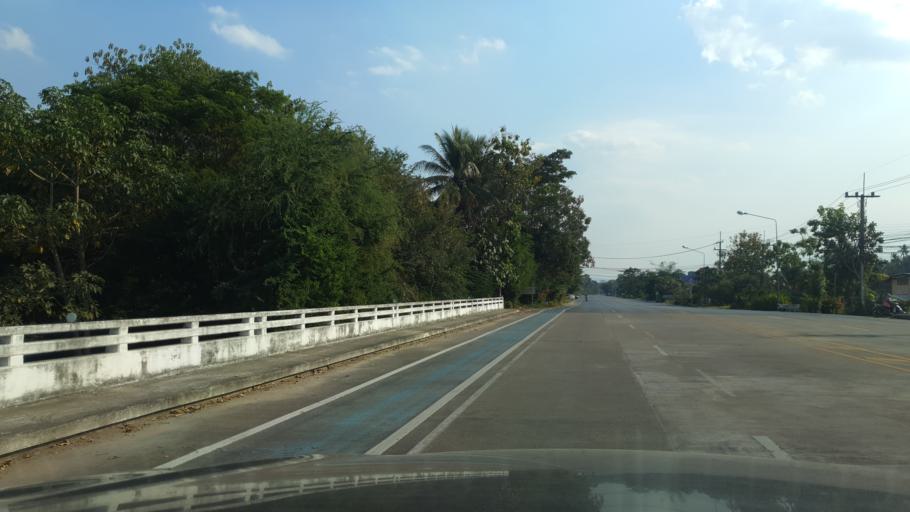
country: TH
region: Tak
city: Tak
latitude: 16.8656
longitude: 99.1200
